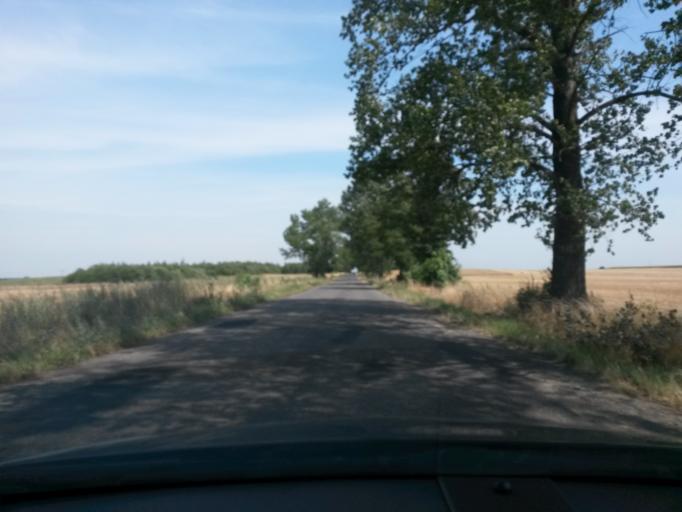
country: PL
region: Lower Silesian Voivodeship
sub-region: Powiat legnicki
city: Prochowice
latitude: 51.1905
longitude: 16.3419
